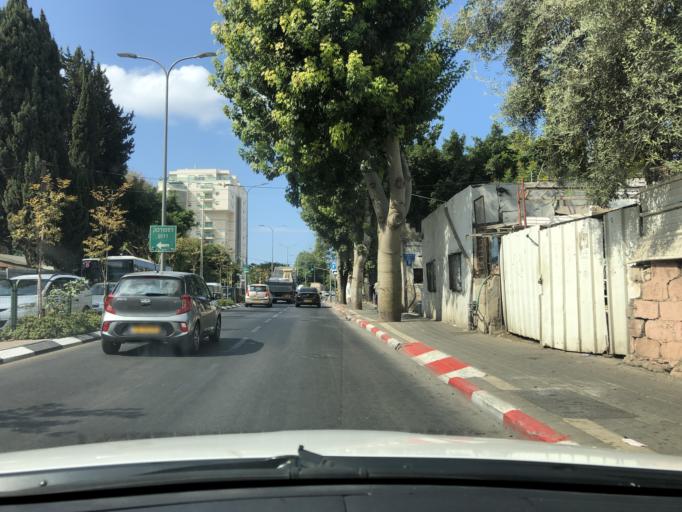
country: IL
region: Tel Aviv
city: Azor
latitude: 32.0476
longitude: 34.7934
